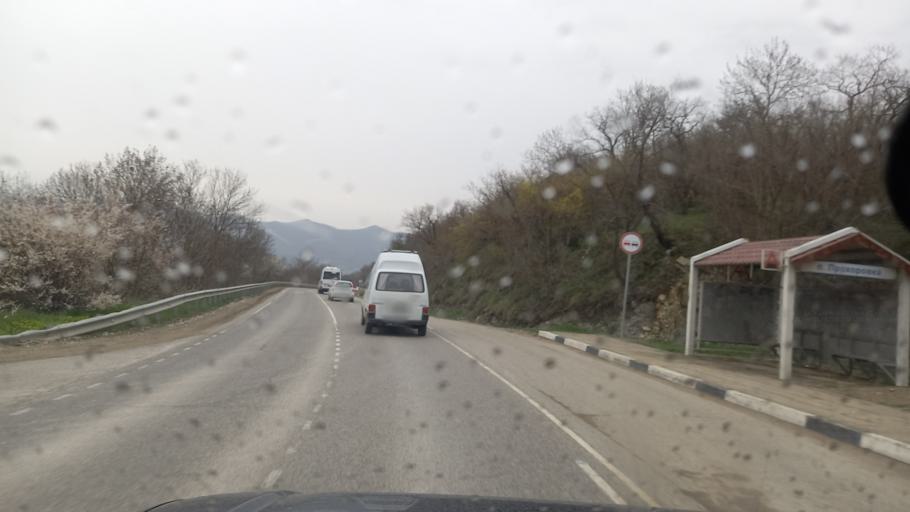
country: RU
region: Krasnodarskiy
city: Gayduk
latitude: 44.7410
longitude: 37.6840
